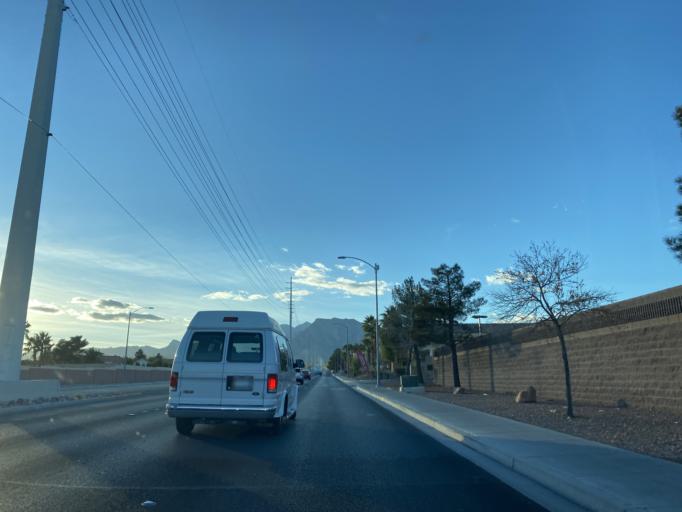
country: US
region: Nevada
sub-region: Clark County
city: Summerlin South
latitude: 36.2187
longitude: -115.2827
